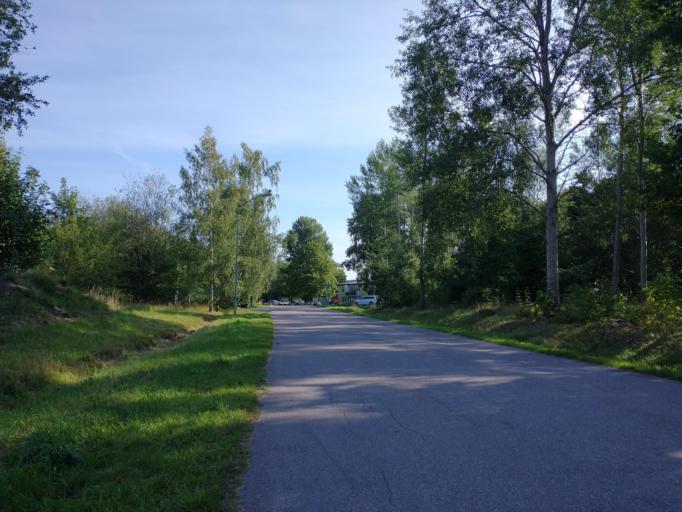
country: SE
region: Kalmar
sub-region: Kalmar Kommun
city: Lindsdal
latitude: 56.7836
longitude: 16.2965
